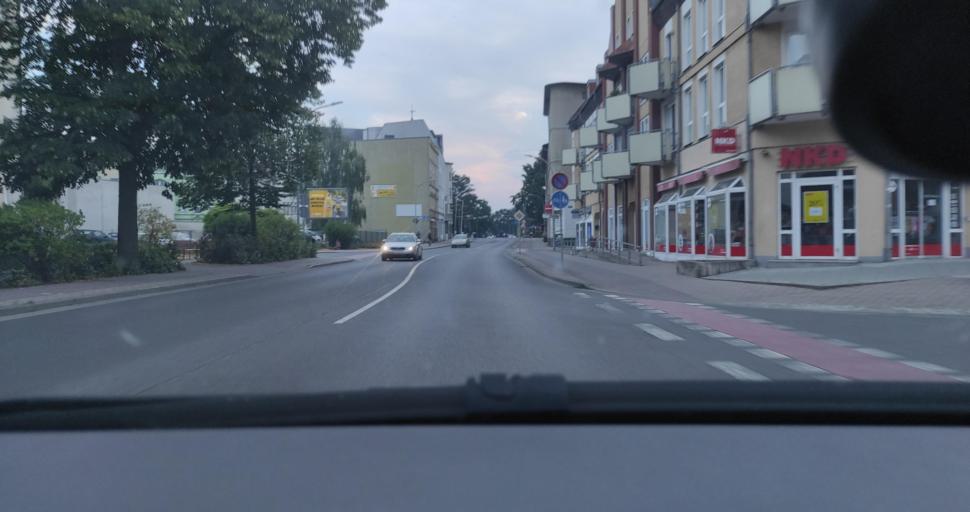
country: DE
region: Brandenburg
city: Forst
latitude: 51.7404
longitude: 14.6421
